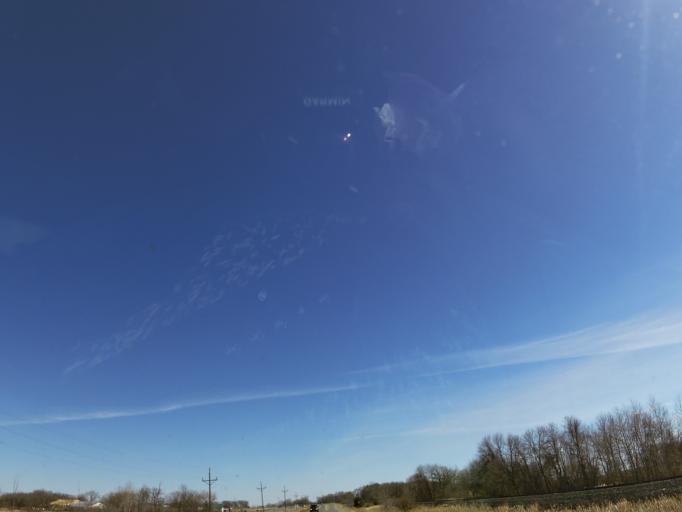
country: US
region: Minnesota
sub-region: Wright County
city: Annandale
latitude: 45.2468
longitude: -94.0841
